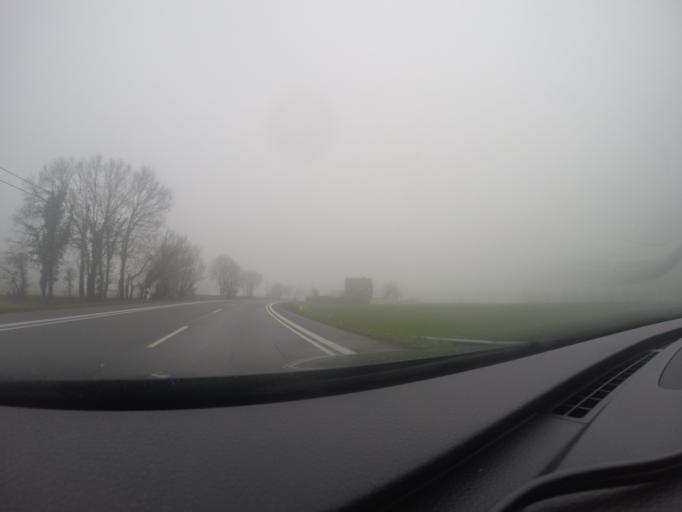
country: DE
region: North Rhine-Westphalia
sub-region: Regierungsbezirk Dusseldorf
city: Bocholt
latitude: 51.8767
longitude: 6.5912
